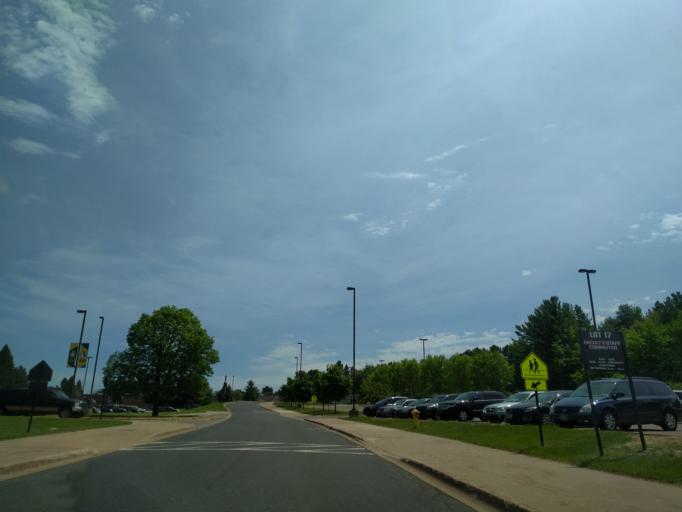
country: US
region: Michigan
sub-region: Marquette County
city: Marquette
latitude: 46.5582
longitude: -87.4087
